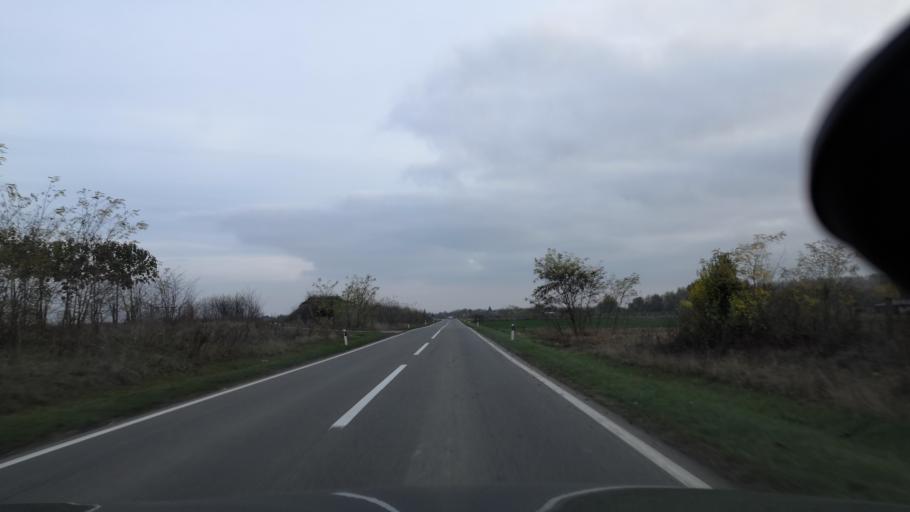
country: RS
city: Sanad
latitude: 45.9924
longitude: 20.1072
